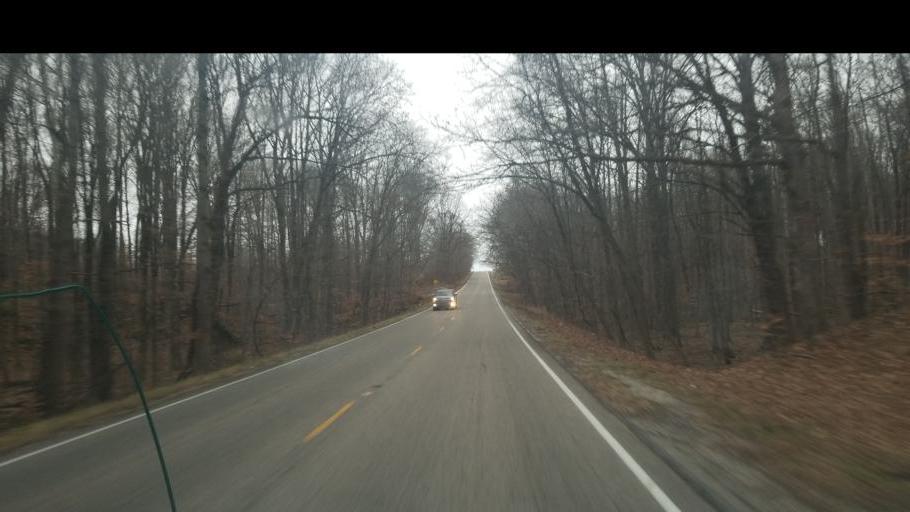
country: US
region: Indiana
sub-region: Clay County
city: Middlebury
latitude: 39.3648
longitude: -86.9641
